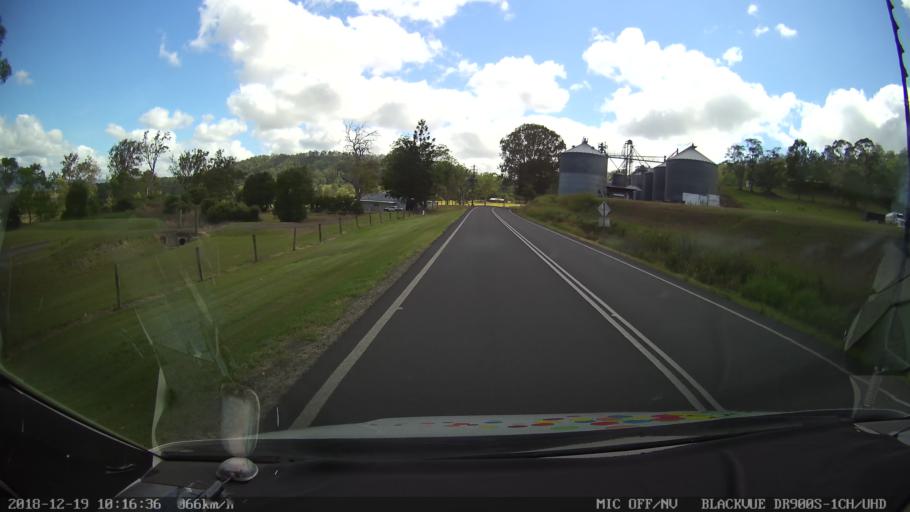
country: AU
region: New South Wales
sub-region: Kyogle
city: Kyogle
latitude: -28.6070
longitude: 153.0230
